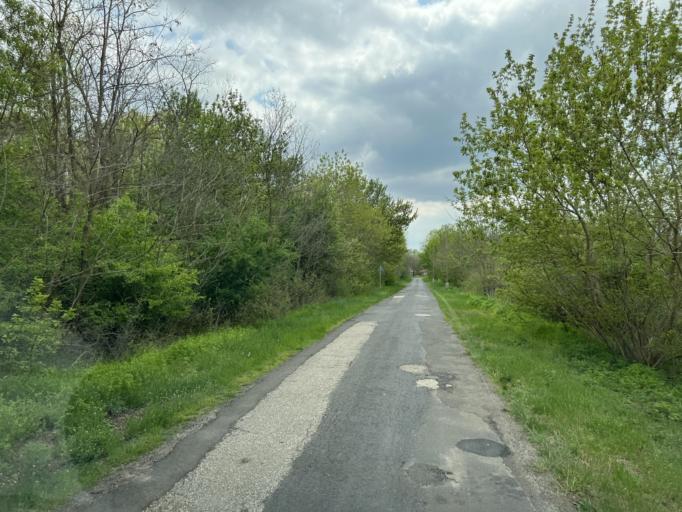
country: HU
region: Pest
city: Orkeny
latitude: 47.0452
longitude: 19.3503
